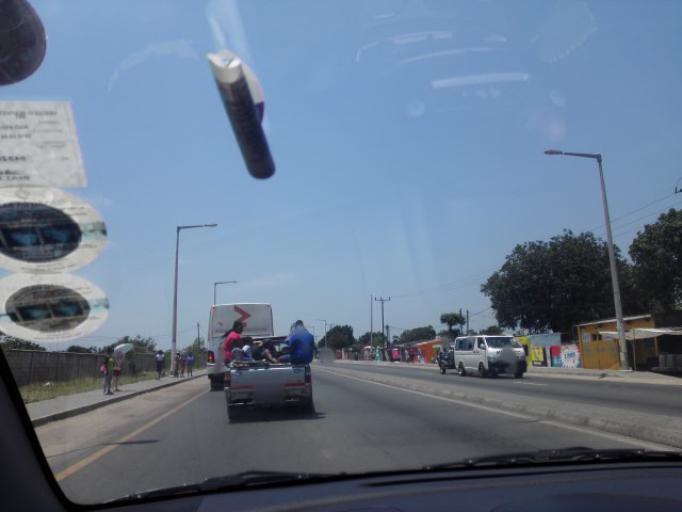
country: MZ
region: Maputo City
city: Maputo
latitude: -25.9149
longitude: 32.5655
